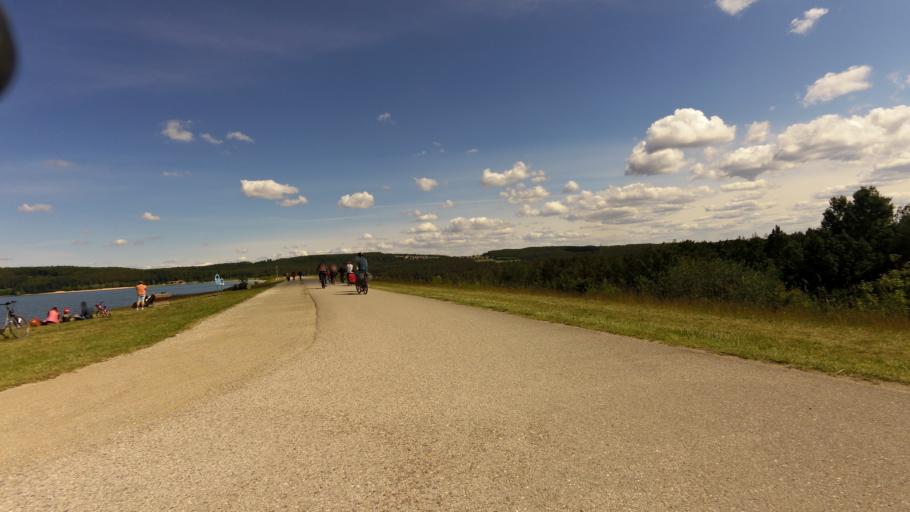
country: DE
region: Bavaria
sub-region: Regierungsbezirk Mittelfranken
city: Pleinfeld
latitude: 49.1199
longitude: 10.9642
